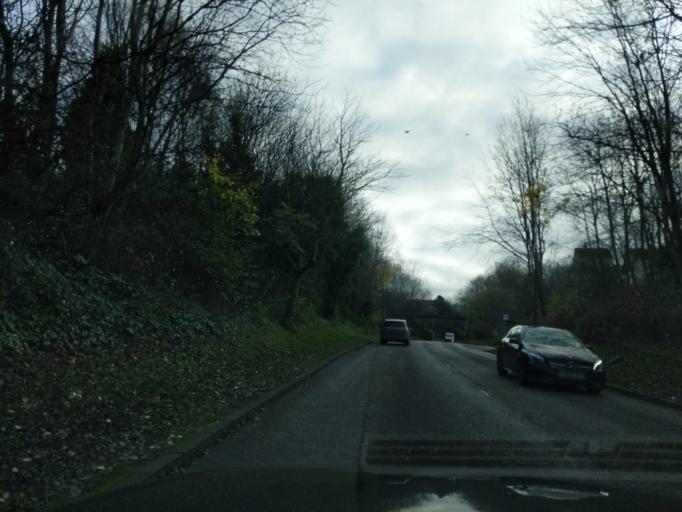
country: GB
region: Scotland
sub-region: Edinburgh
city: Colinton
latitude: 55.9206
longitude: -3.2766
